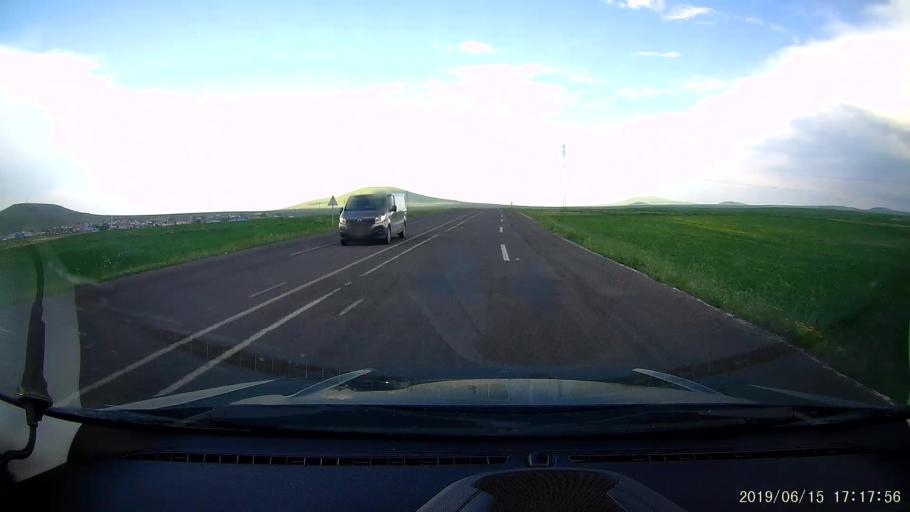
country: TR
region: Kars
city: Kars
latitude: 40.6144
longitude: 43.2480
